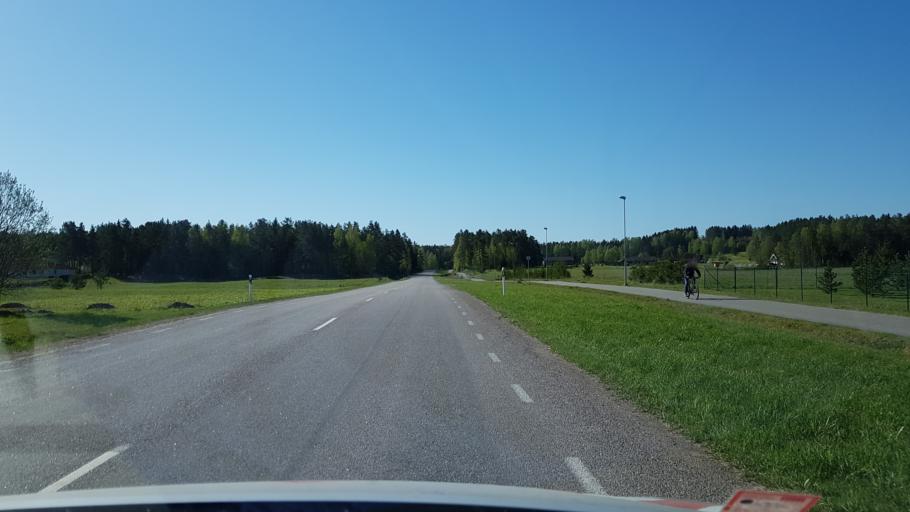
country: EE
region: Vorumaa
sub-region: Voru linn
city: Voru
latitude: 57.8092
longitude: 27.0320
